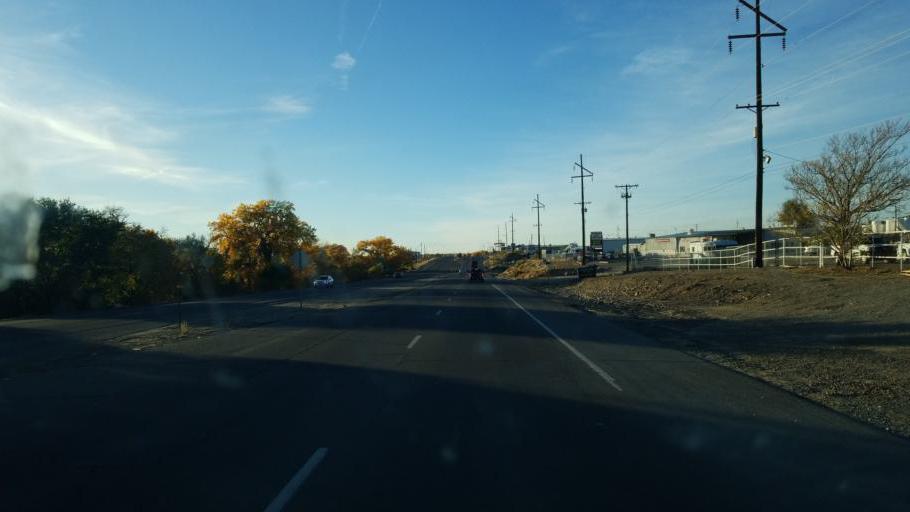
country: US
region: New Mexico
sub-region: San Juan County
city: Farmington
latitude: 36.7144
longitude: -108.1477
